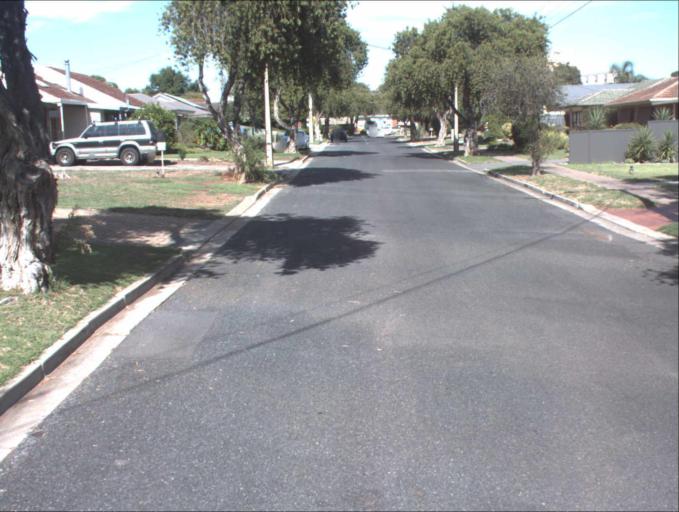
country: AU
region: South Australia
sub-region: Port Adelaide Enfield
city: Gilles Plains
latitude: -34.8654
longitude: 138.6527
